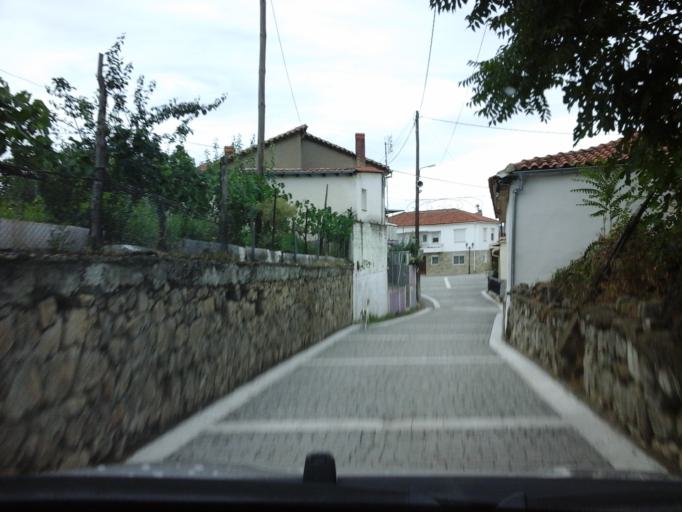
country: GR
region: East Macedonia and Thrace
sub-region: Nomos Evrou
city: Soufli
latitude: 41.1288
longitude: 26.2258
